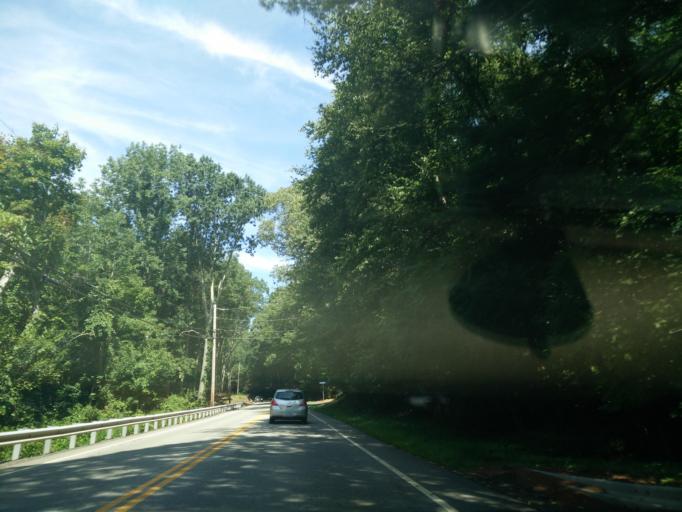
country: US
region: Connecticut
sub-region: Middlesex County
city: Clinton
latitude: 41.3212
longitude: -72.5444
